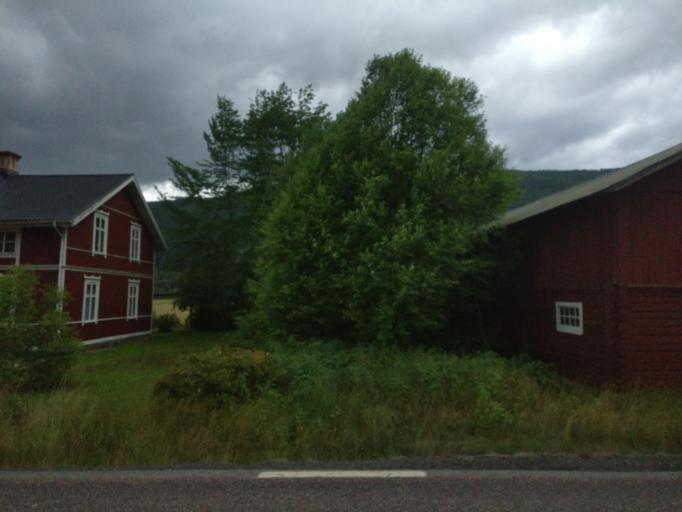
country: SE
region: Vaermland
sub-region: Torsby Kommun
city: Torsby
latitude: 60.7087
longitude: 12.8919
